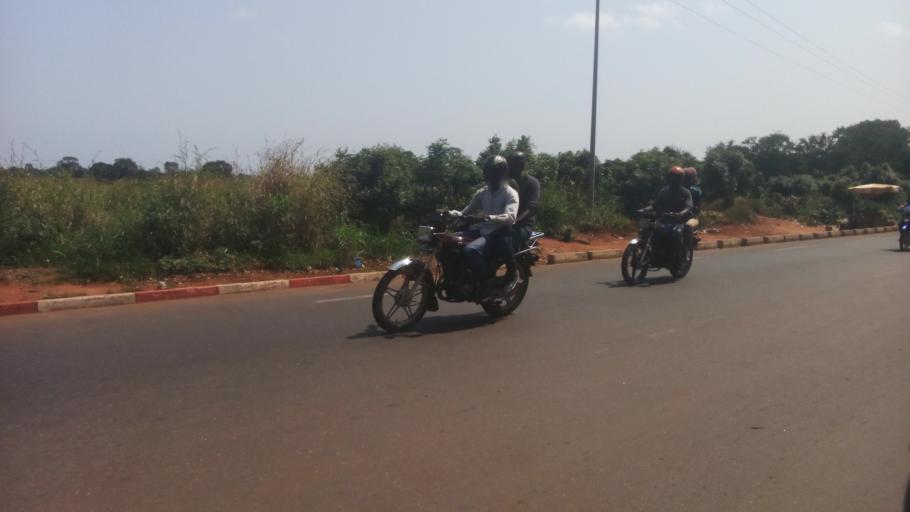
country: TG
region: Maritime
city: Lome
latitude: 6.1919
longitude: 1.2301
